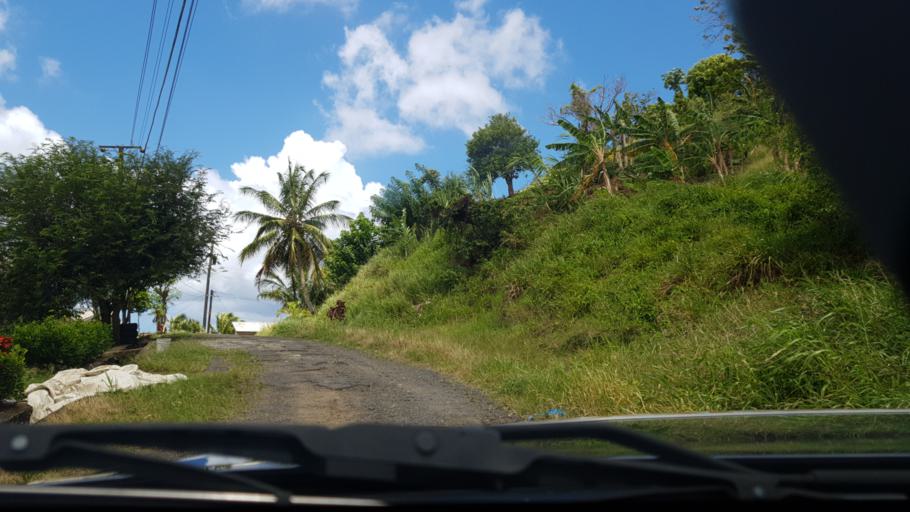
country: LC
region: Anse-la-Raye
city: Anse La Raye
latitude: 13.9503
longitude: -60.9934
